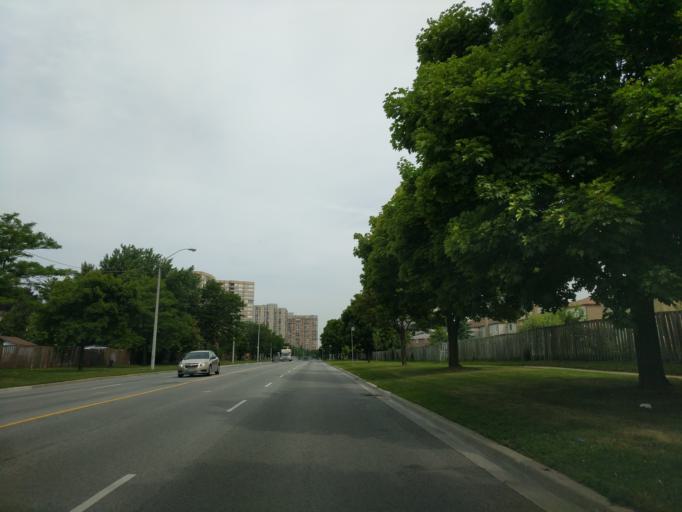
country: CA
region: Ontario
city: Scarborough
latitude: 43.8096
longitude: -79.3224
